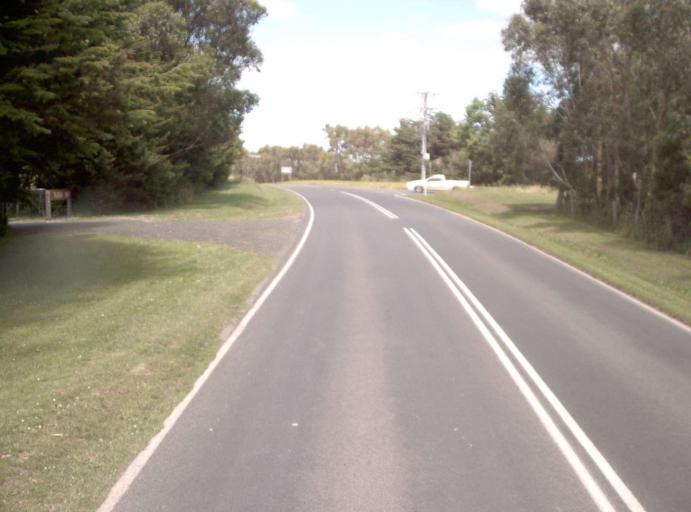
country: AU
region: Victoria
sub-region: Bass Coast
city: North Wonthaggi
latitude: -38.7020
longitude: 146.0873
